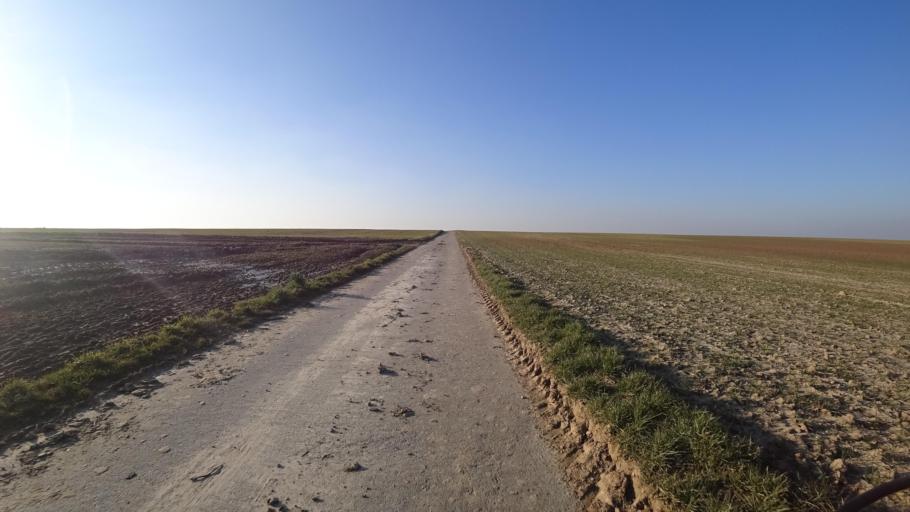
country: BE
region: Wallonia
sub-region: Province du Brabant Wallon
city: Chaumont-Gistoux
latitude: 50.6411
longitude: 4.7457
